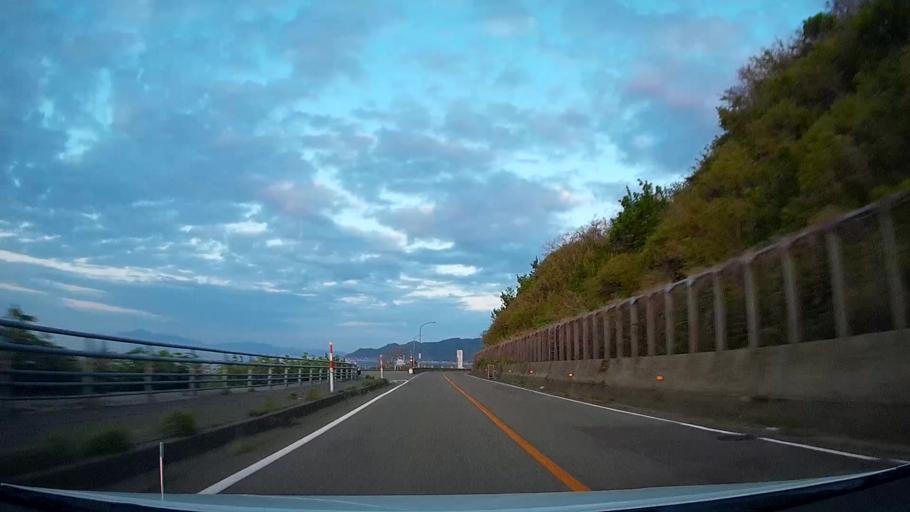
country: JP
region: Niigata
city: Joetsu
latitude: 37.1703
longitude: 138.1208
